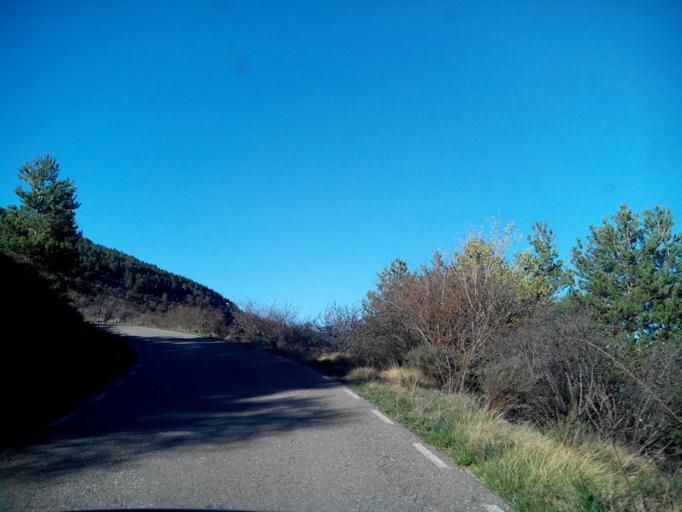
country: ES
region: Catalonia
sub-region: Provincia de Barcelona
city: Saldes
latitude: 42.2259
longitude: 1.7276
